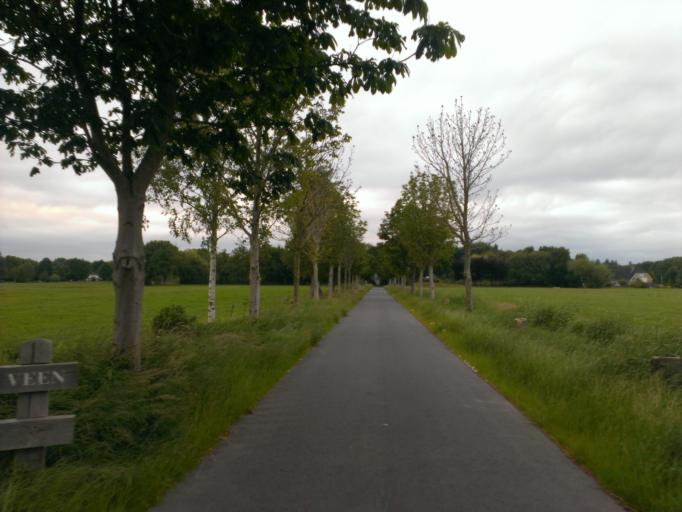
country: NL
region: Gelderland
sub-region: Gemeente Heerde
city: Heerde
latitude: 52.3915
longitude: 6.0211
